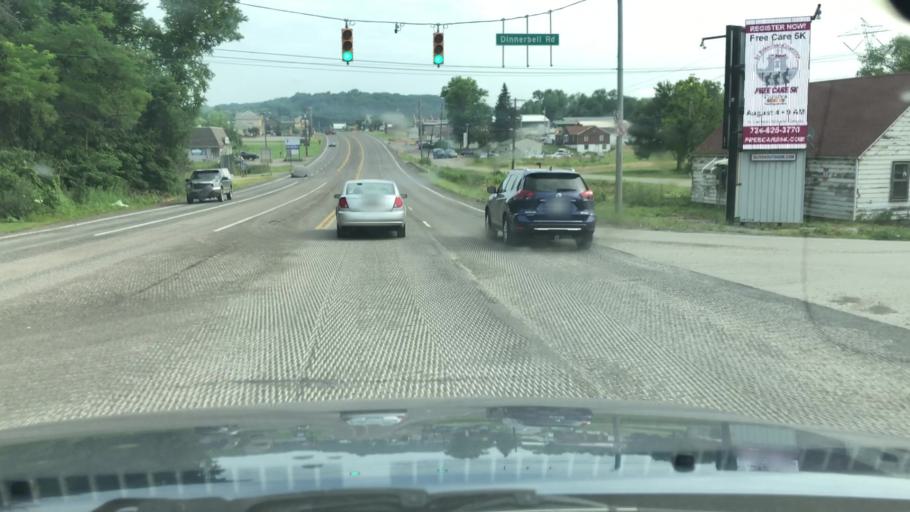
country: US
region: Pennsylvania
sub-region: Butler County
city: Nixon
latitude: 40.7566
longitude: -79.9241
